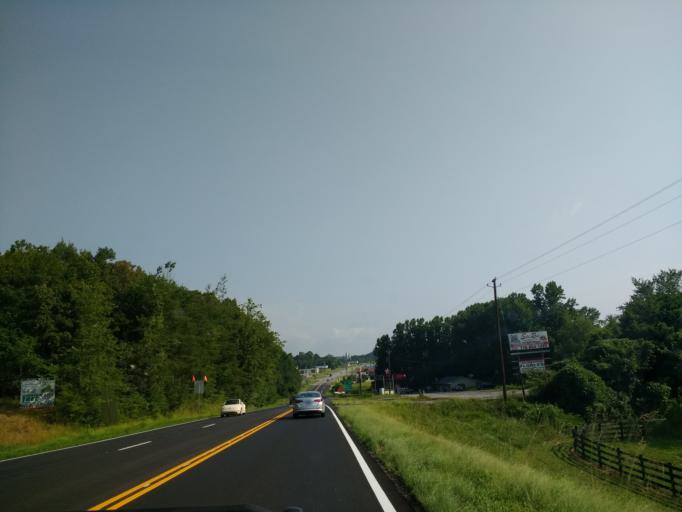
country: US
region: Georgia
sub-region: White County
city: Cleveland
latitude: 34.5011
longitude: -83.7564
